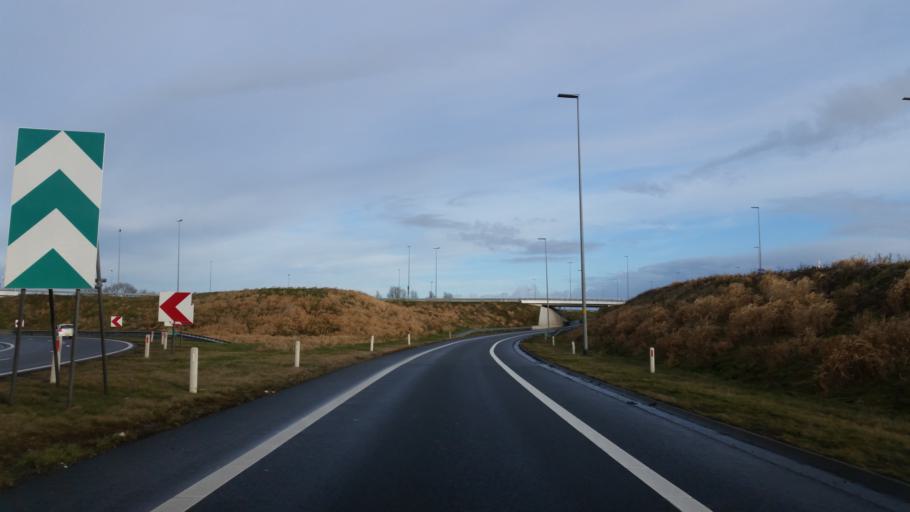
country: NL
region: Friesland
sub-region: Gemeente Leeuwarden
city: Wirdum
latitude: 53.1570
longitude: 5.7921
